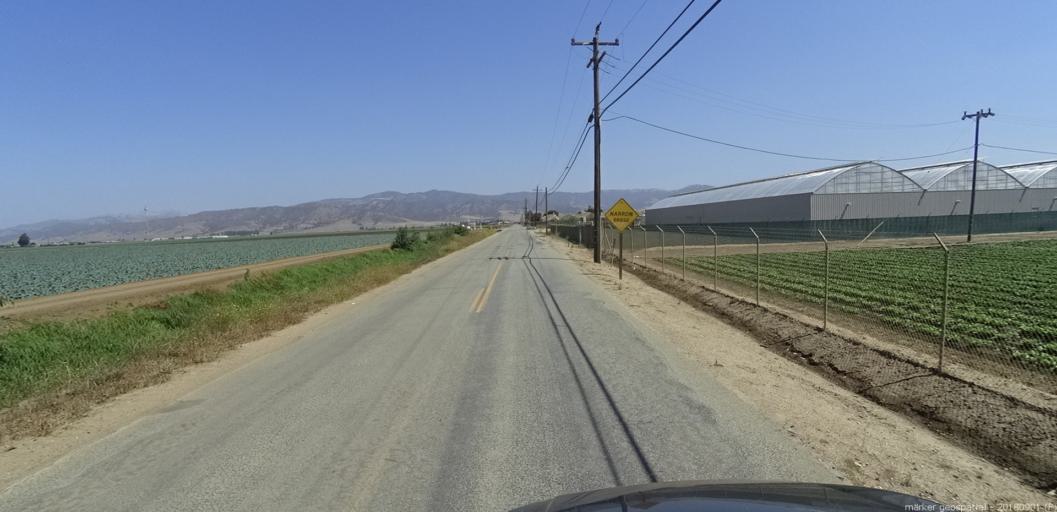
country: US
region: California
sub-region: Monterey County
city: Chualar
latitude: 36.6107
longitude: -121.5496
